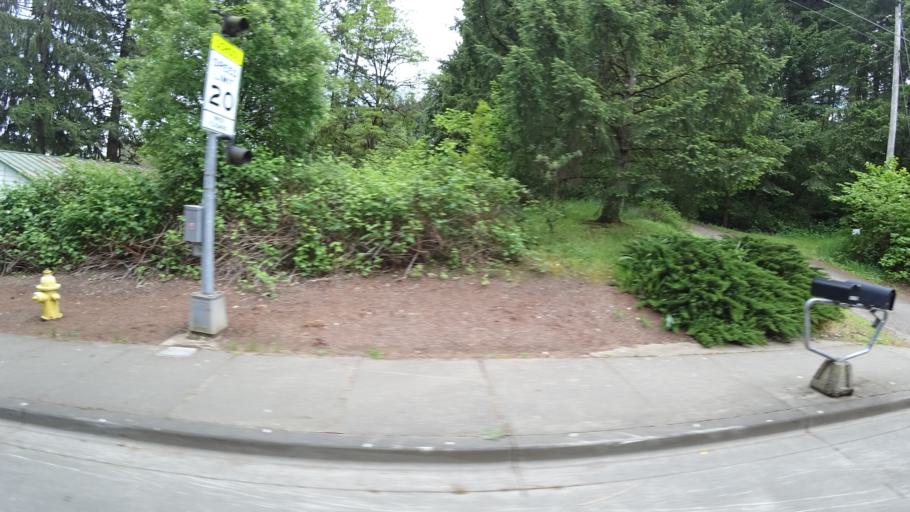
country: US
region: Oregon
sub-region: Washington County
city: Aloha
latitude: 45.4750
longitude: -122.8393
